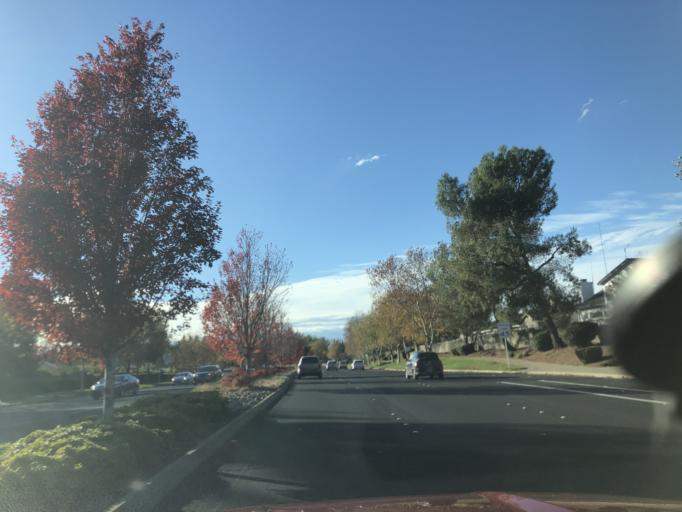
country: US
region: California
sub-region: Placer County
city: Roseville
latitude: 38.7757
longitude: -121.2945
